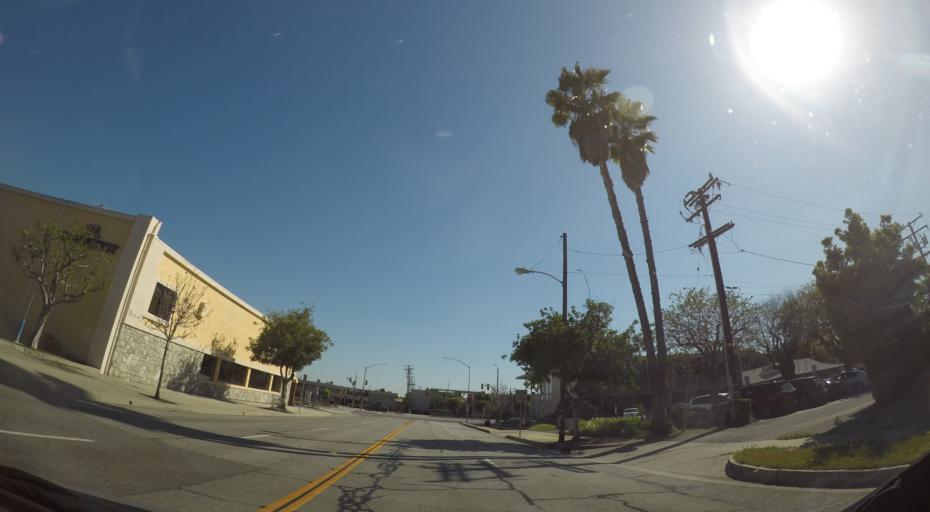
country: US
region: California
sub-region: Los Angeles County
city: Temple City
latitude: 34.1317
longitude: -118.0675
